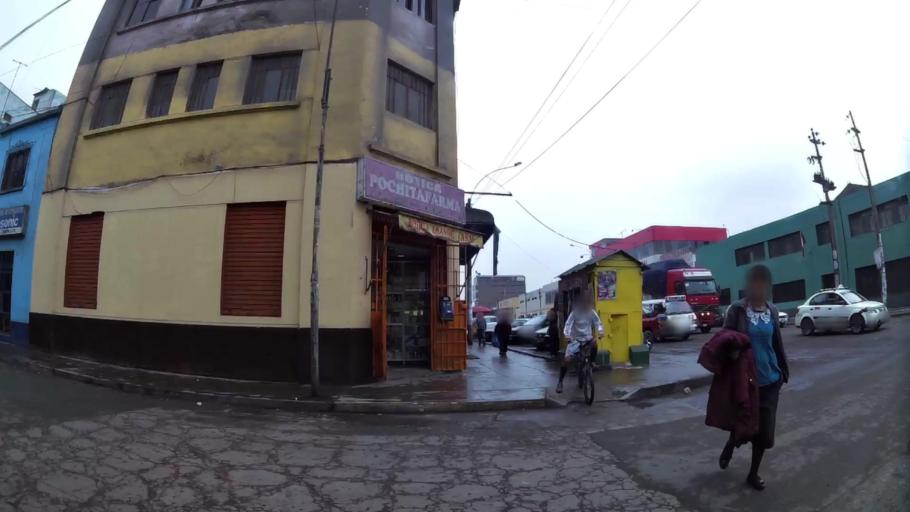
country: PE
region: Lima
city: Lima
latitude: -12.0623
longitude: -77.0237
